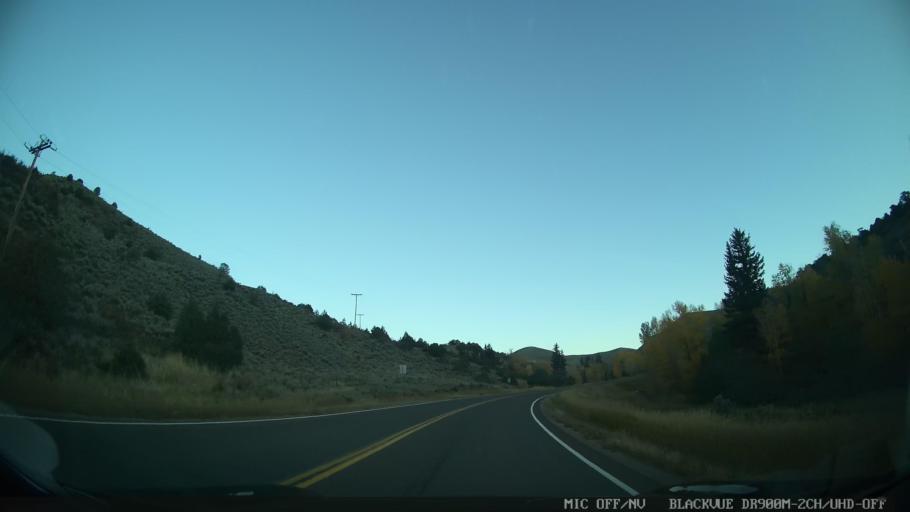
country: US
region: Colorado
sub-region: Eagle County
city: Edwards
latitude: 39.7614
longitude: -106.6771
